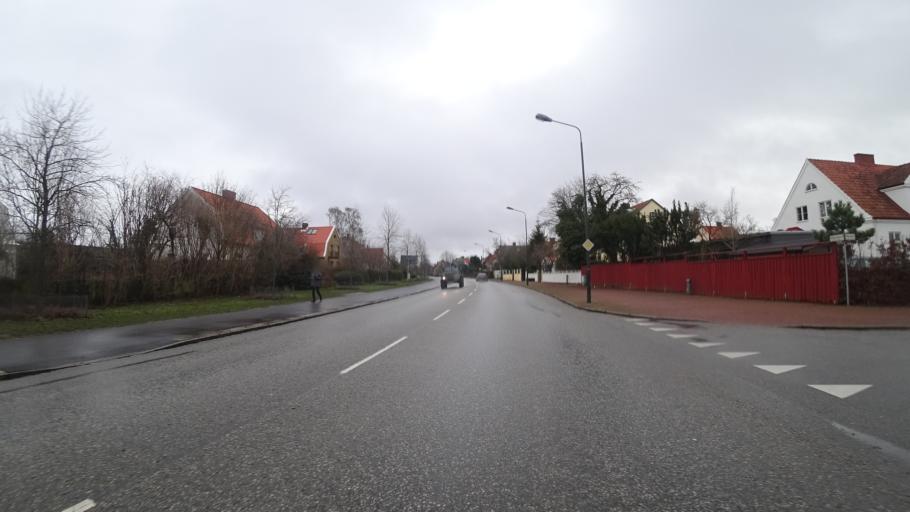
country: SE
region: Skane
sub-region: Malmo
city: Malmoe
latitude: 55.5879
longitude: 12.9650
